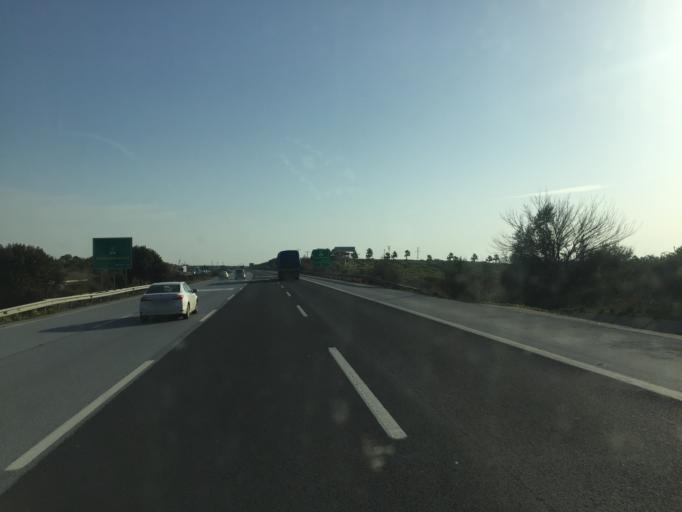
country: TR
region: Mersin
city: Yenice
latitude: 37.0228
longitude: 35.0925
